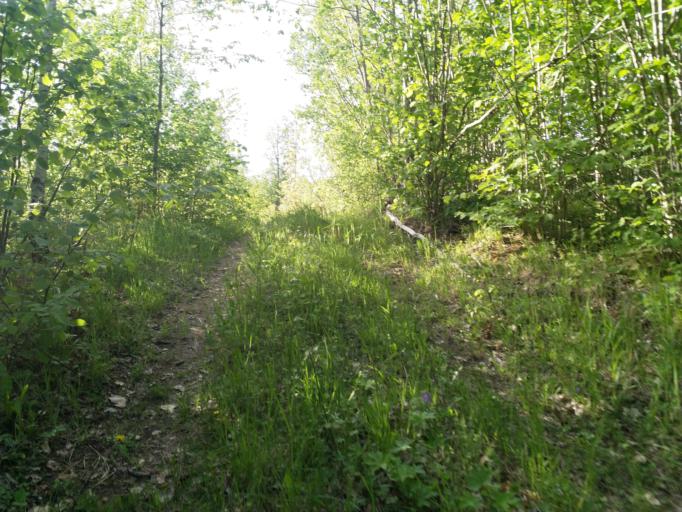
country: LV
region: Kuldigas Rajons
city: Kuldiga
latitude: 56.8572
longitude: 21.8643
